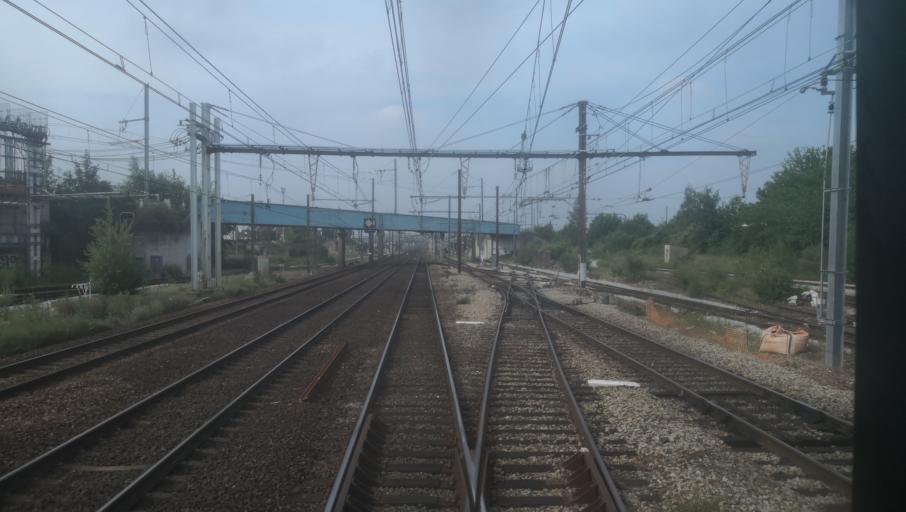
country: FR
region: Ile-de-France
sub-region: Departement de l'Essonne
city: Bretigny-sur-Orge
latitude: 48.5970
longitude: 2.2969
